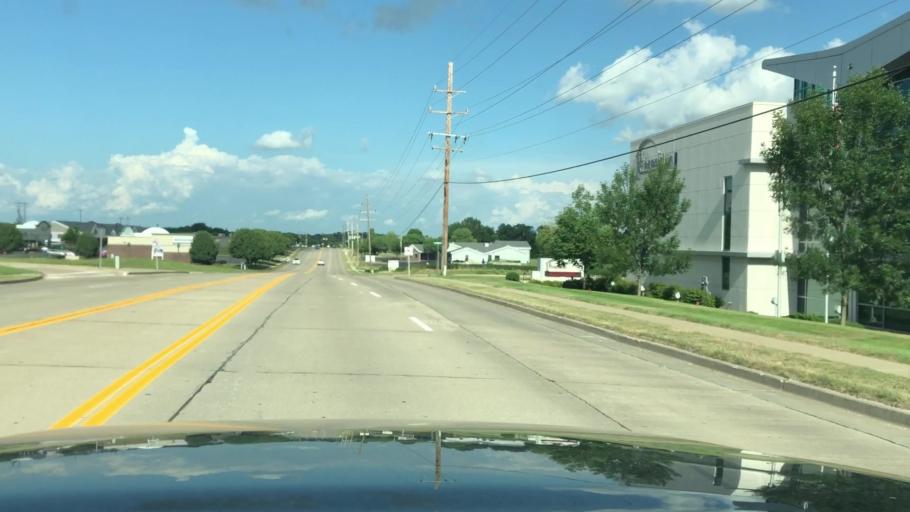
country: US
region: Missouri
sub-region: Saint Charles County
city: Wentzville
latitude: 38.8248
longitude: -90.8661
